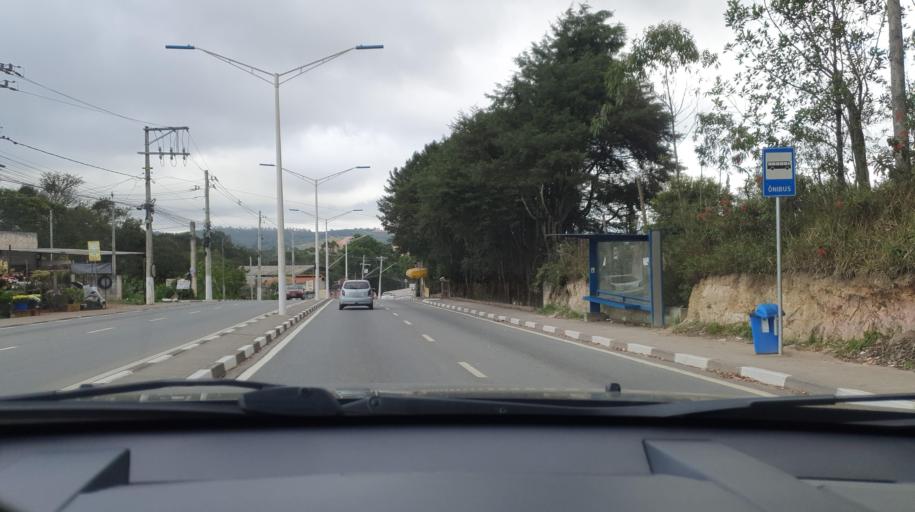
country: BR
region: Sao Paulo
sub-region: Vargem Grande Paulista
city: Vargem Grande Paulista
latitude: -23.6779
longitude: -47.0150
